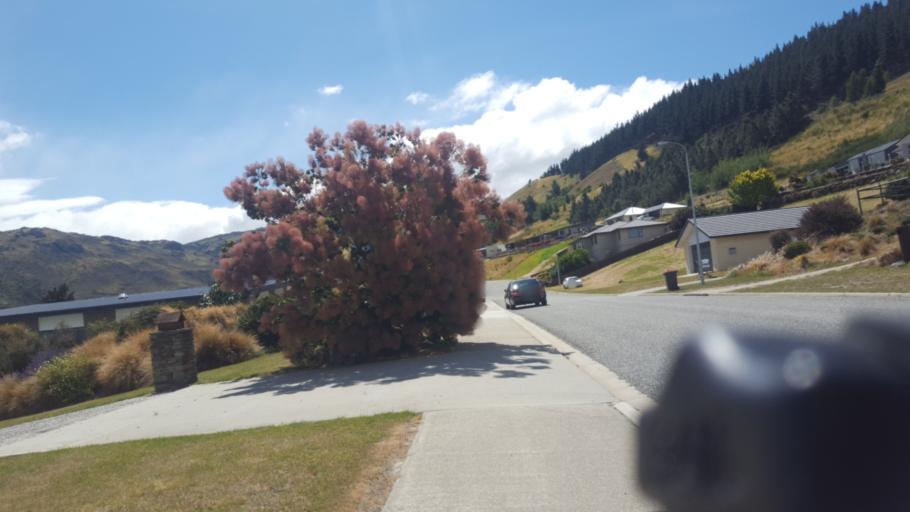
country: NZ
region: Otago
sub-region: Queenstown-Lakes District
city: Wanaka
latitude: -45.1882
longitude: 169.3265
